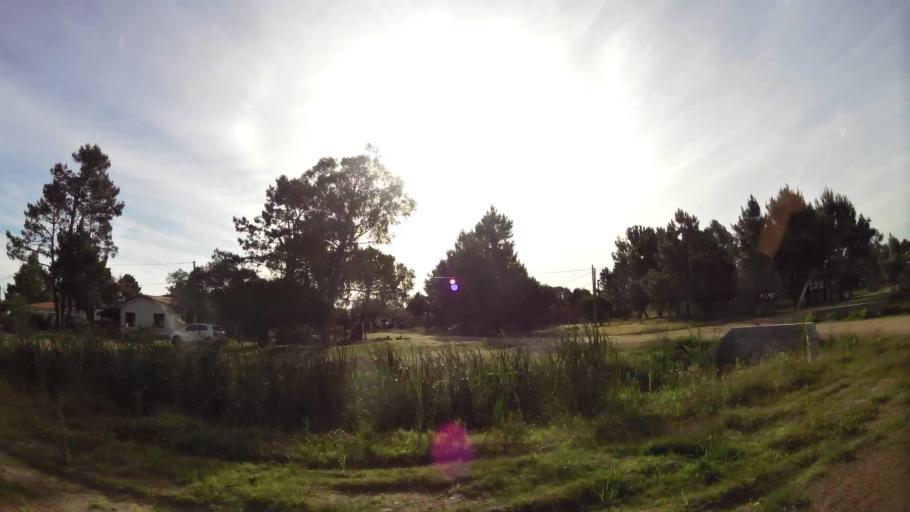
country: UY
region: Canelones
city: Atlantida
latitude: -34.7846
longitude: -55.8499
